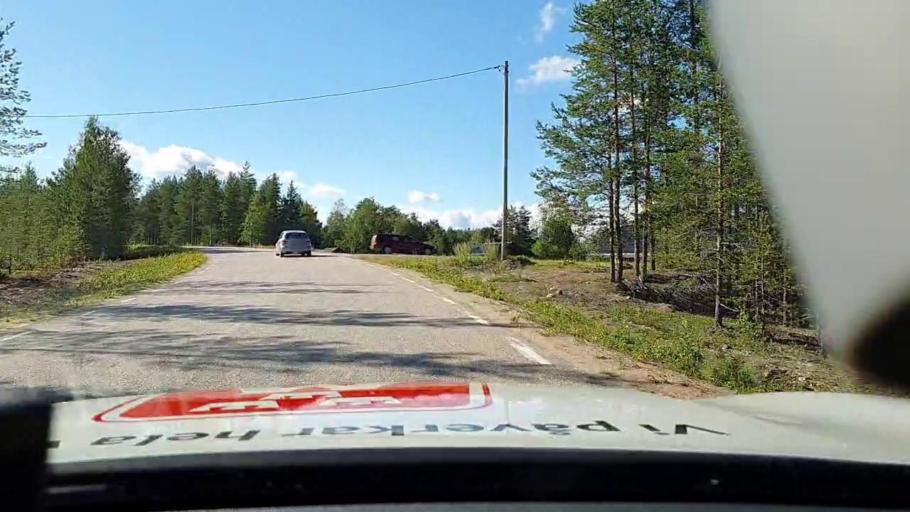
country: SE
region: Norrbotten
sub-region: Overkalix Kommun
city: OEverkalix
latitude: 66.2455
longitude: 22.9211
